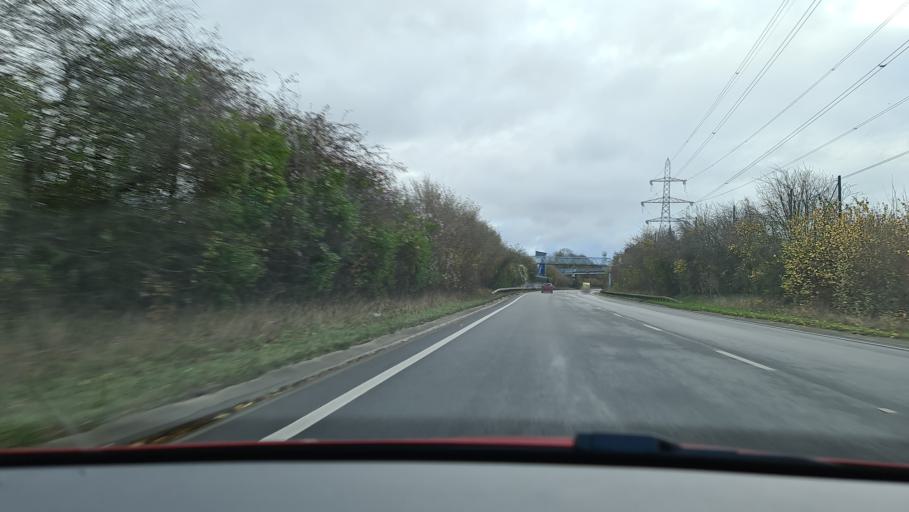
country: GB
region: England
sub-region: Buckinghamshire
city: Wendover
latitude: 51.7628
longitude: -0.7497
